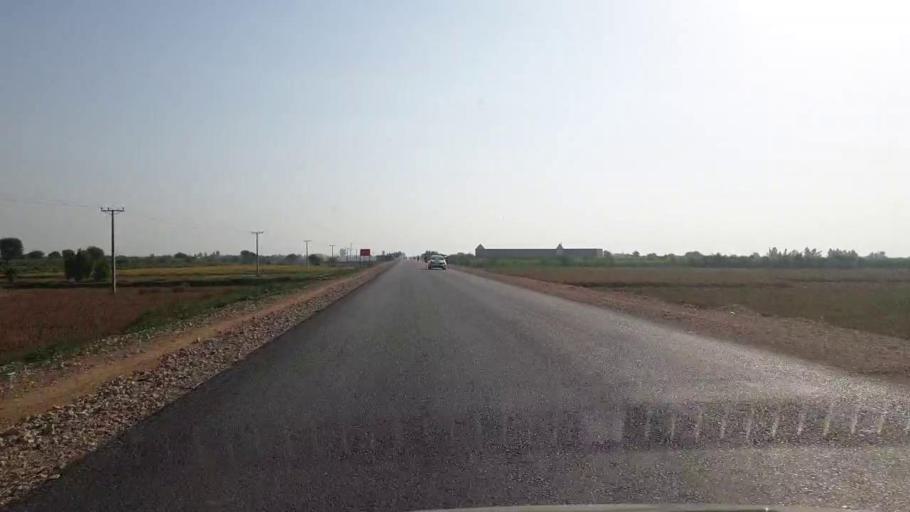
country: PK
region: Sindh
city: Badin
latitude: 24.6600
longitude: 68.8860
